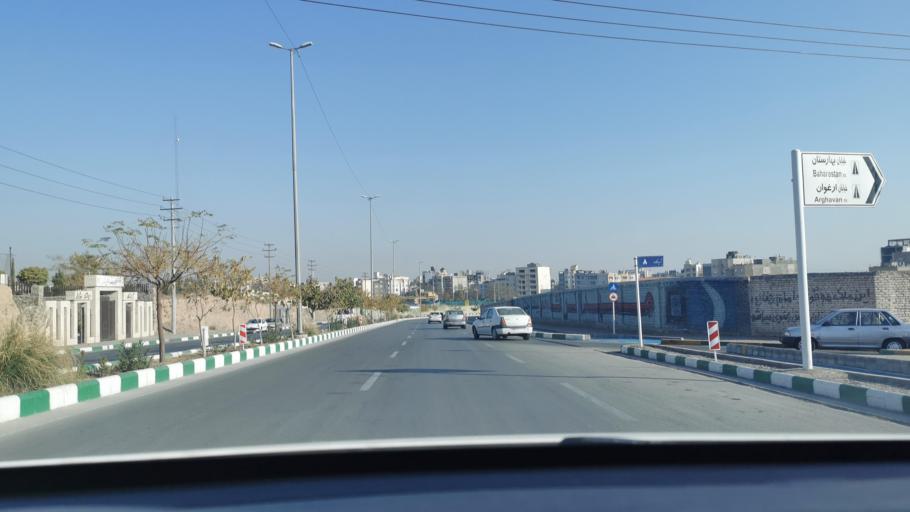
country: IR
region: Razavi Khorasan
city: Mashhad
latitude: 36.2799
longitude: 59.5416
